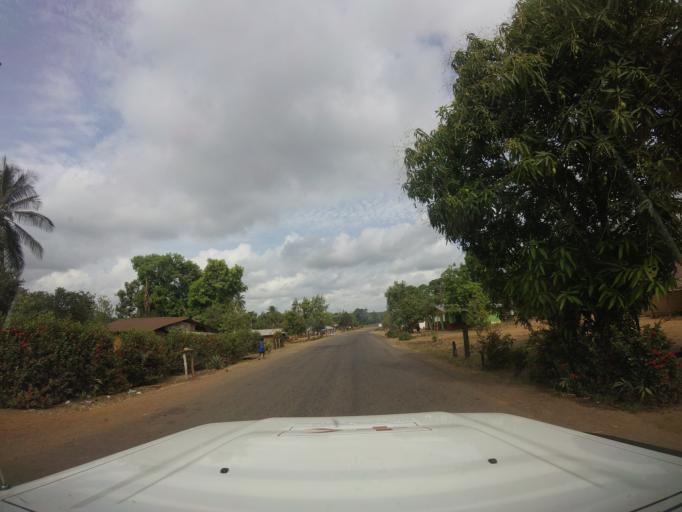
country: LR
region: Bomi
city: Tubmanburg
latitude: 6.7017
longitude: -10.9177
